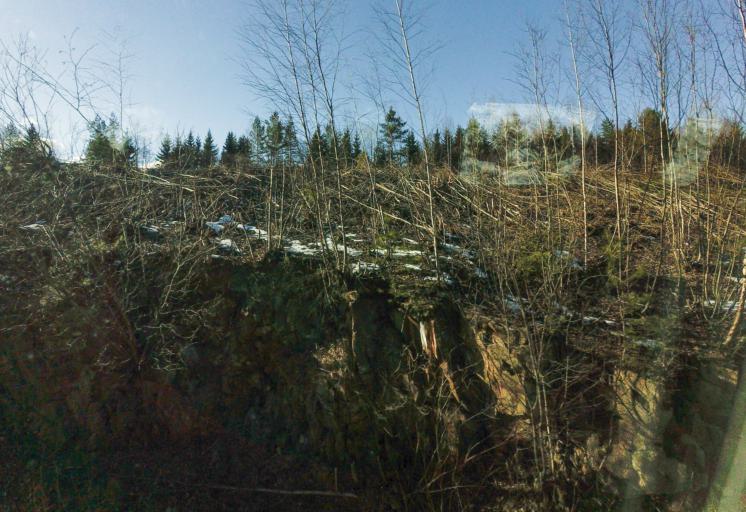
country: FI
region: South Karelia
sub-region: Imatra
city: Parikkala
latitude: 61.5047
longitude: 29.4952
